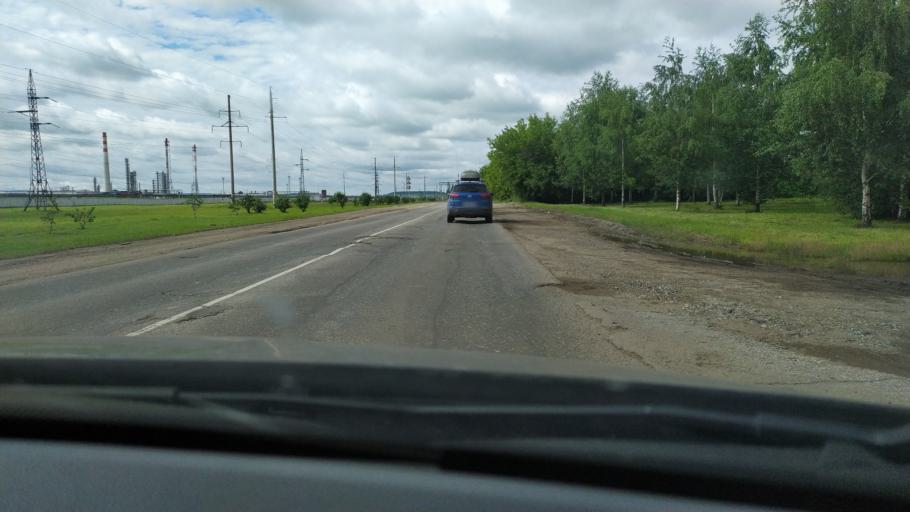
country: RU
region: Perm
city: Kondratovo
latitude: 57.9293
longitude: 56.1201
